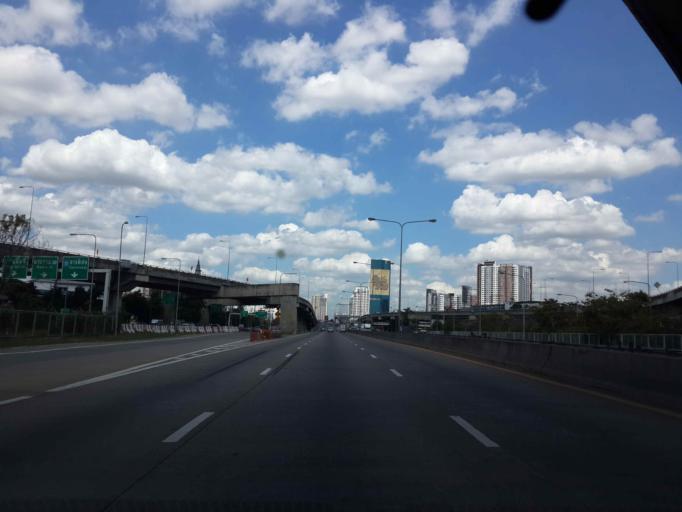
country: TH
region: Bangkok
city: Yan Nawa
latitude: 13.6928
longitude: 100.5271
